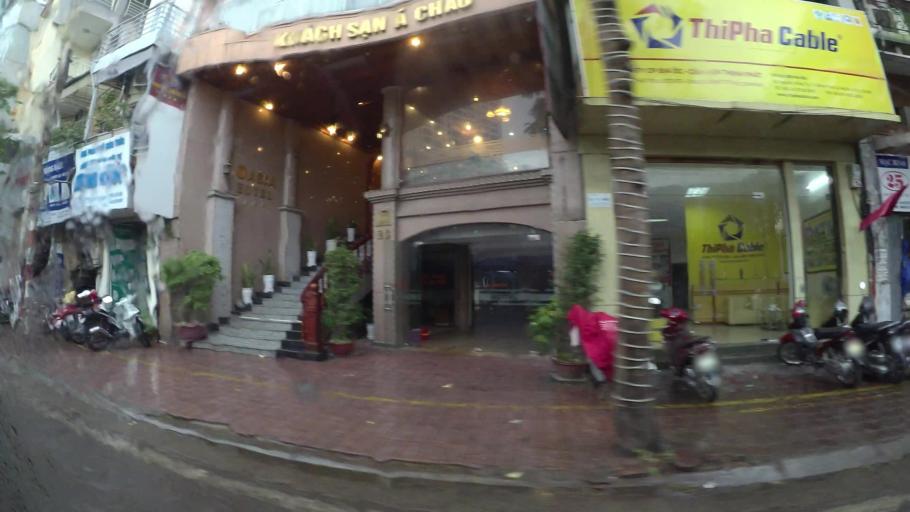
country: VN
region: Ha Noi
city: Hai BaTrung
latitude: 21.0141
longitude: 105.8565
